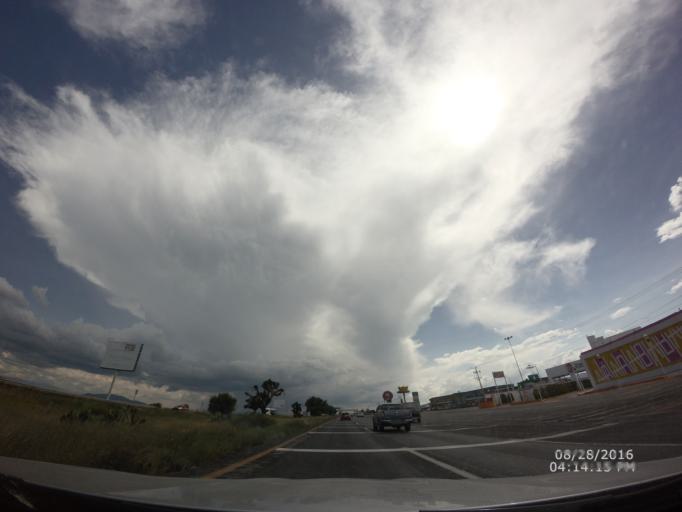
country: MX
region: Hidalgo
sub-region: Zempoala
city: El Mirador
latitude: 20.0110
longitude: -98.8207
